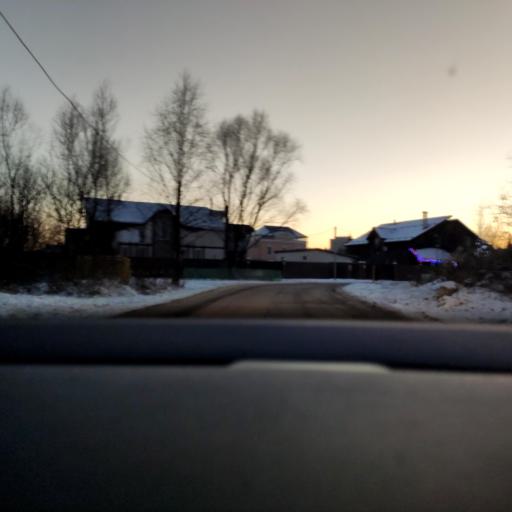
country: RU
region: Moskovskaya
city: Skhodnya
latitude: 55.8935
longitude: 37.3047
